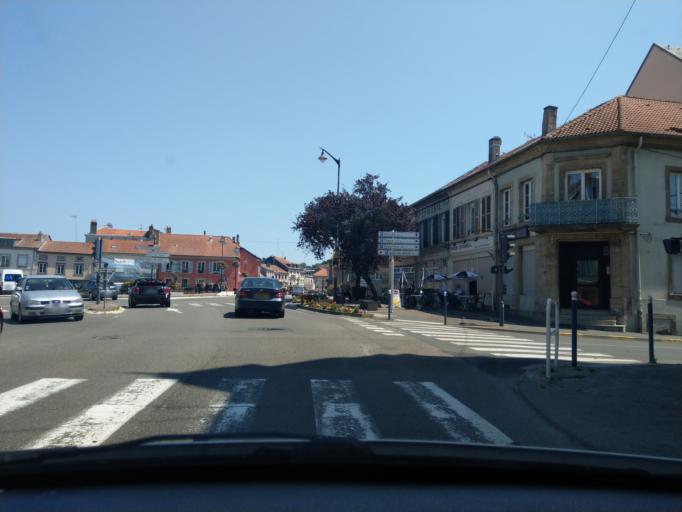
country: FR
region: Lorraine
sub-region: Departement de la Moselle
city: Sarrebourg
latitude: 48.7351
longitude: 7.0492
